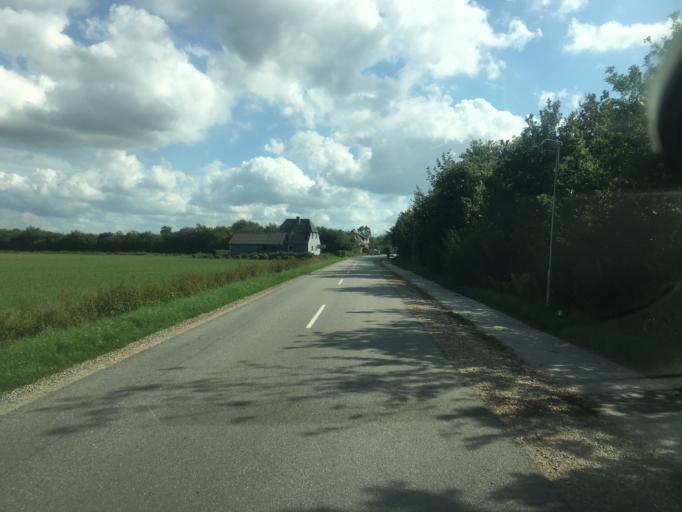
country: DE
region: Schleswig-Holstein
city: Ellhoft
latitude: 54.9432
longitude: 8.9676
